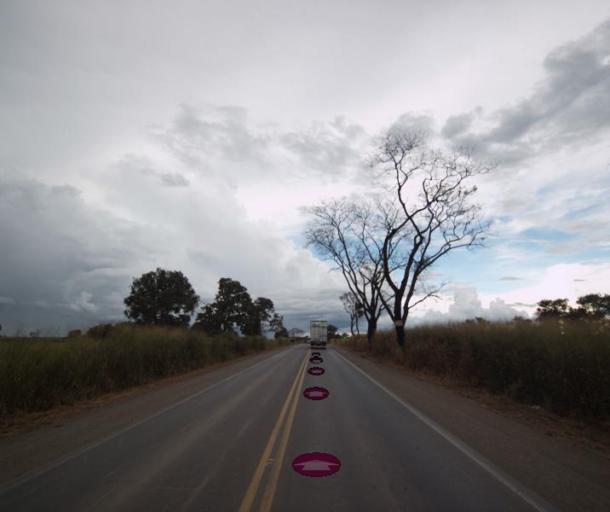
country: BR
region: Goias
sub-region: Itapaci
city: Itapaci
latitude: -14.9066
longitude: -49.3518
